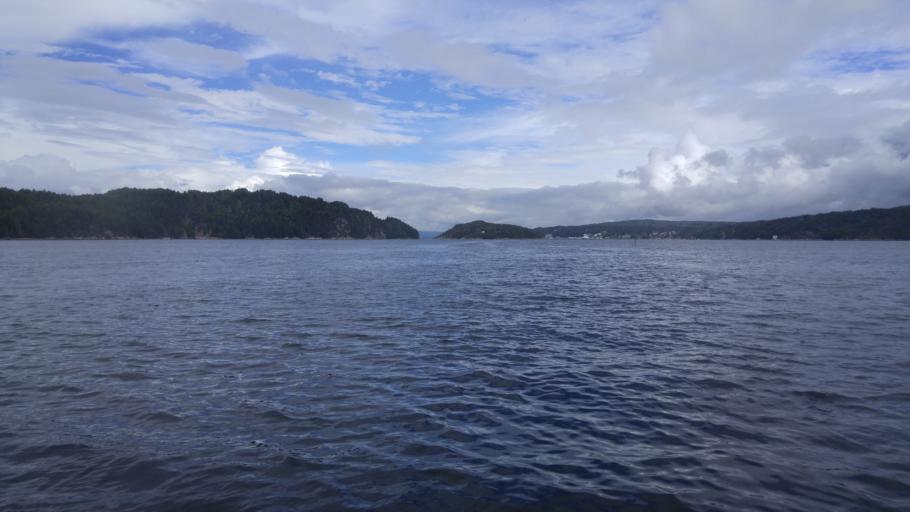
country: NO
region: Akershus
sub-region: Nesodden
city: Fagerstrand
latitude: 59.7025
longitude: 10.5698
